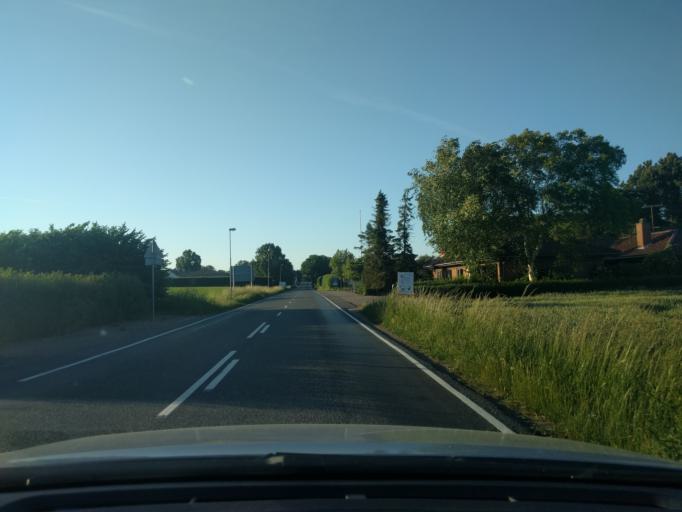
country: DK
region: South Denmark
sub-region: Kerteminde Kommune
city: Kerteminde
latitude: 55.4977
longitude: 10.6495
